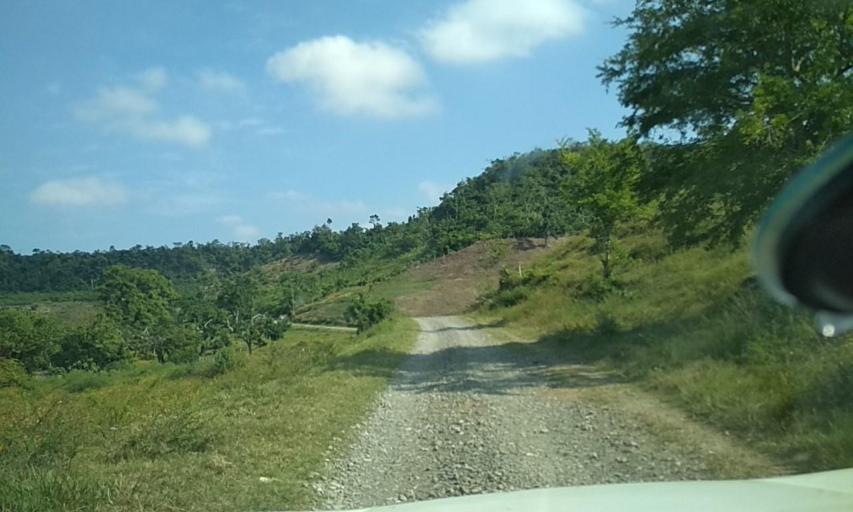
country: MX
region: Veracruz
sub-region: Cazones de Herrera
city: Rancho Nuevo
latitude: 20.6245
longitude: -97.2241
